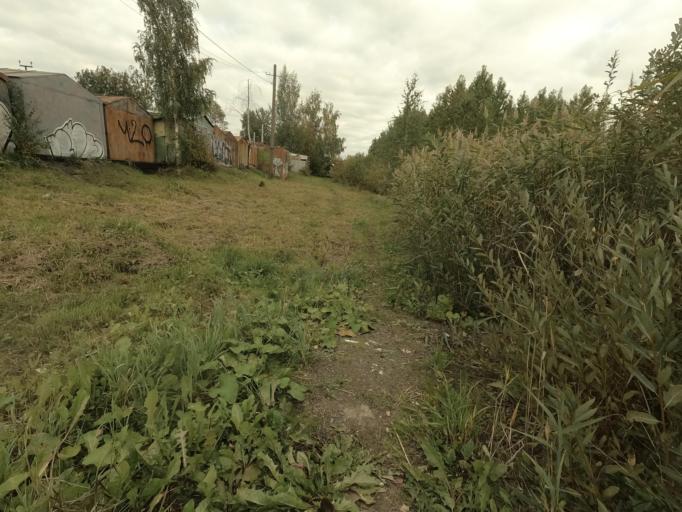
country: RU
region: Leningrad
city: Rybatskoye
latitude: 59.8356
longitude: 30.4915
